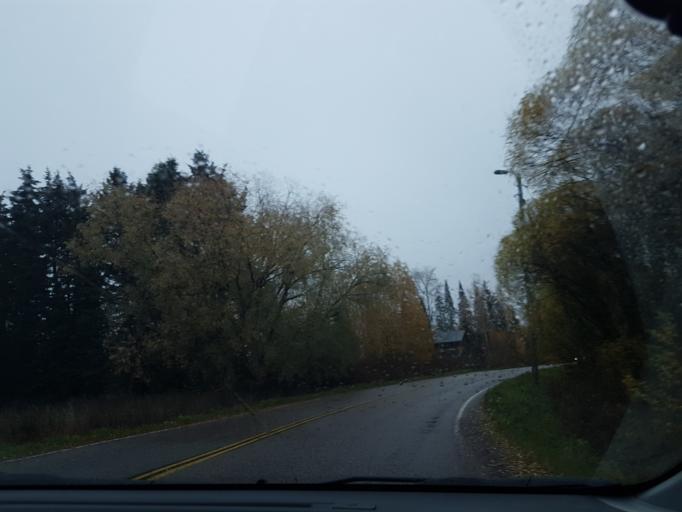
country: FI
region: Uusimaa
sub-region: Helsinki
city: Maentsaelae
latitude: 60.6176
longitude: 25.2413
